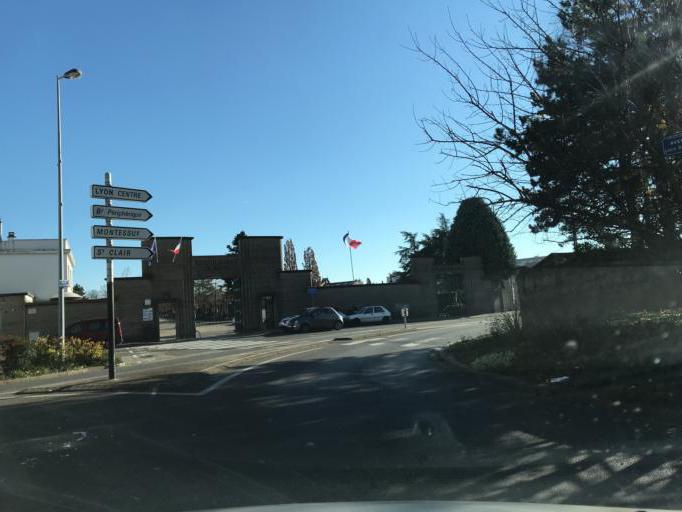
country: FR
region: Rhone-Alpes
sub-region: Departement du Rhone
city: Caluire-et-Cuire
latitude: 45.8027
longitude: 4.8512
